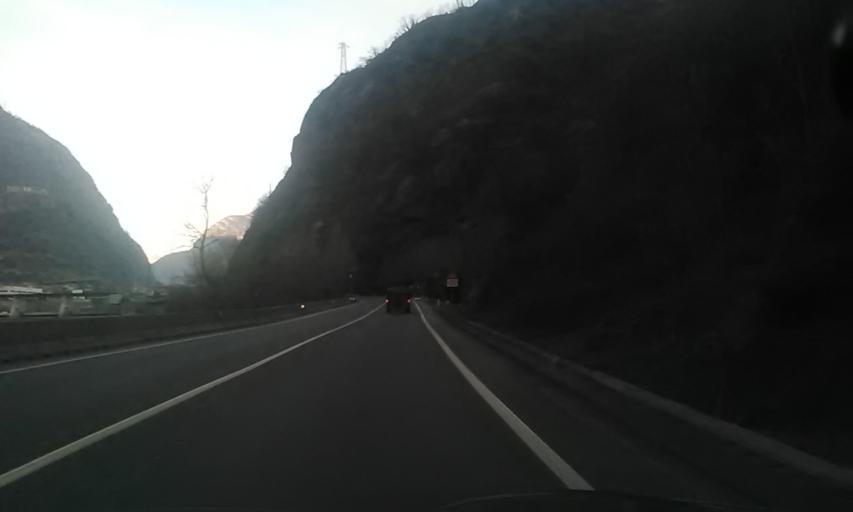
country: IT
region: Aosta Valley
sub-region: Valle d'Aosta
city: Bard
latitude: 45.6052
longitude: 7.7445
